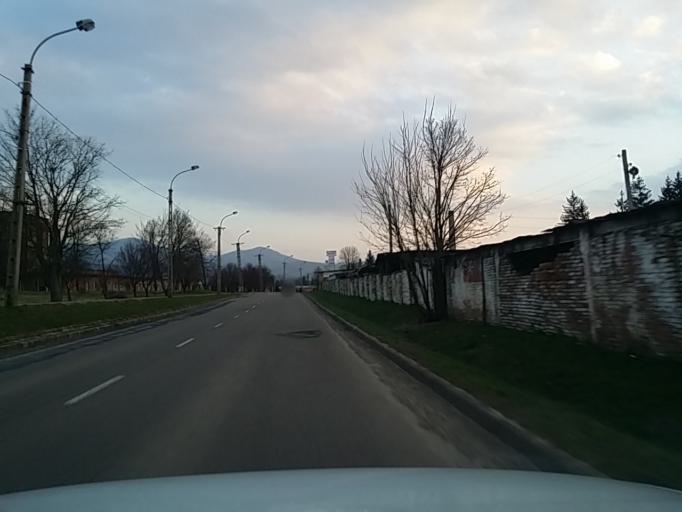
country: HU
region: Nograd
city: Batonyterenye
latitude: 47.9829
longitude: 19.8233
